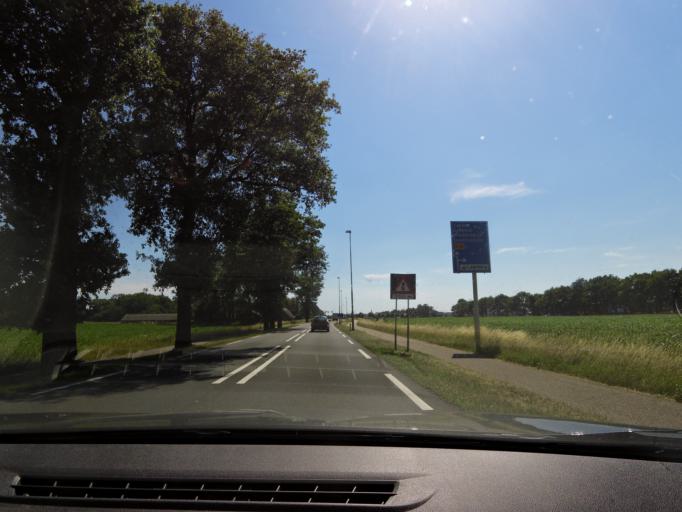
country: NL
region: Gelderland
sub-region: Berkelland
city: Eibergen
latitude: 52.0641
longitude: 6.6307
